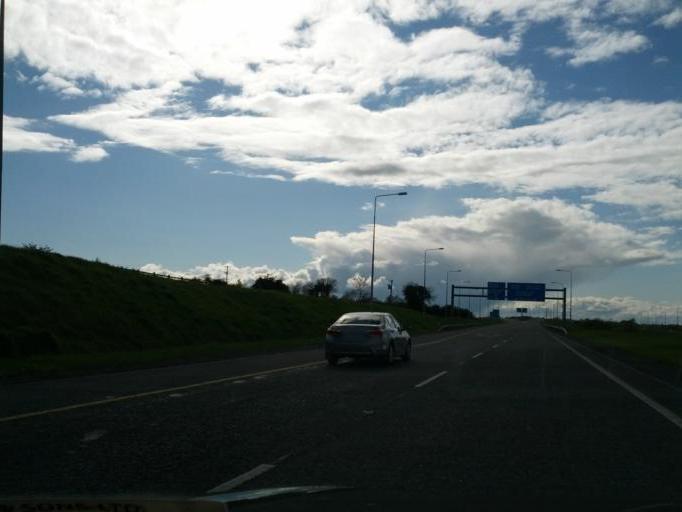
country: IE
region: Leinster
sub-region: An Iarmhi
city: Kinnegad
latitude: 53.4490
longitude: -7.0946
